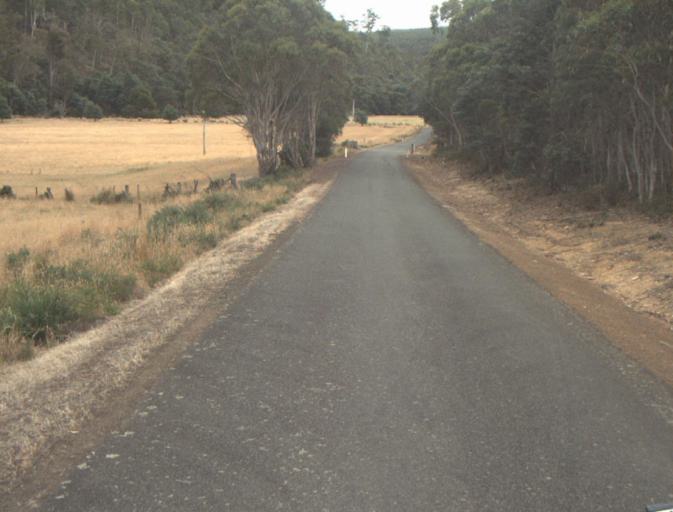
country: AU
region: Tasmania
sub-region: Northern Midlands
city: Evandale
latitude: -41.4690
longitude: 147.4954
